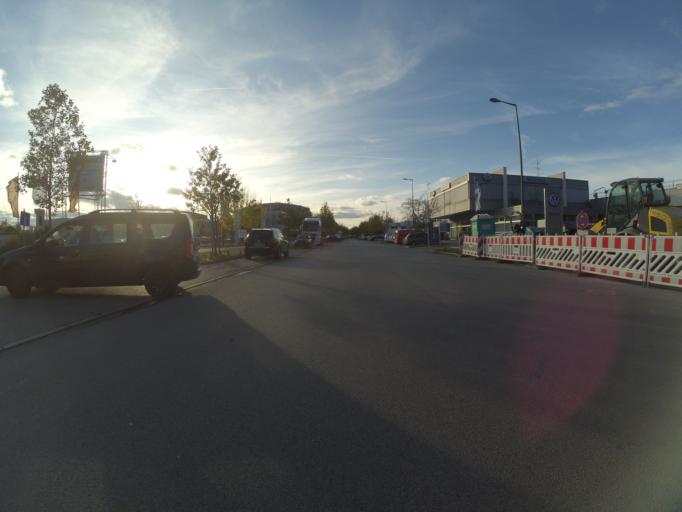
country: DE
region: Bavaria
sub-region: Upper Bavaria
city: Munich
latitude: 48.1926
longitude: 11.5640
